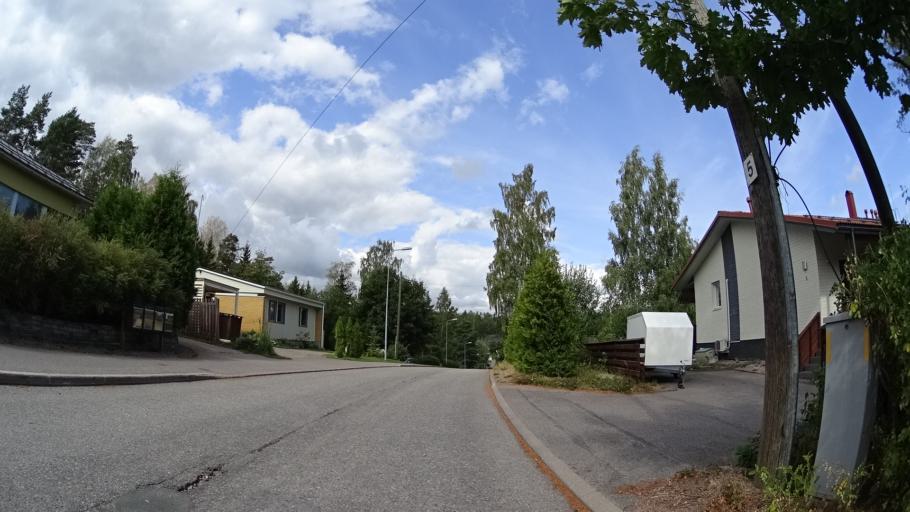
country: FI
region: Uusimaa
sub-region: Helsinki
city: Kilo
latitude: 60.1892
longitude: 24.7592
